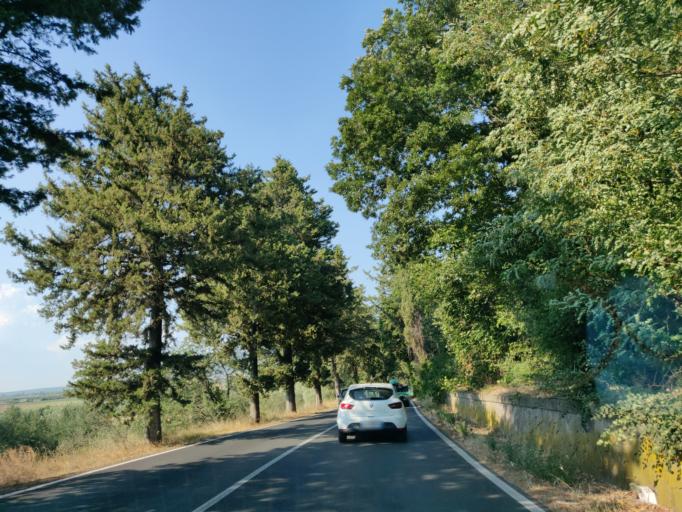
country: IT
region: Latium
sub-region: Provincia di Viterbo
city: Canino
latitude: 42.4040
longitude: 11.6940
